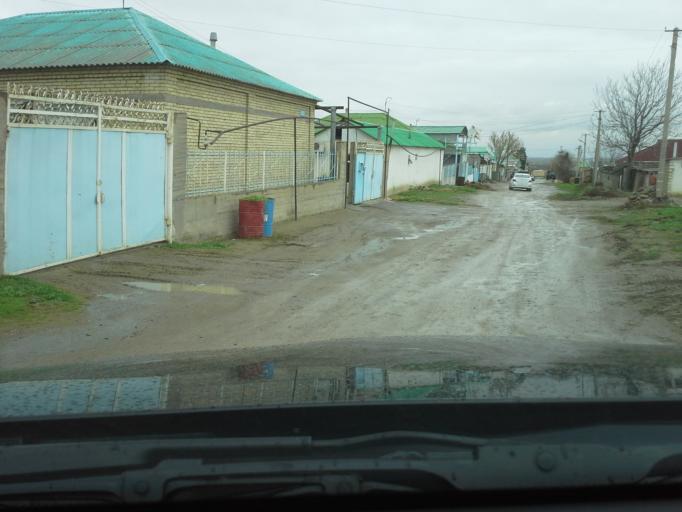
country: TM
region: Ahal
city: Abadan
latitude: 37.9639
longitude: 58.2095
